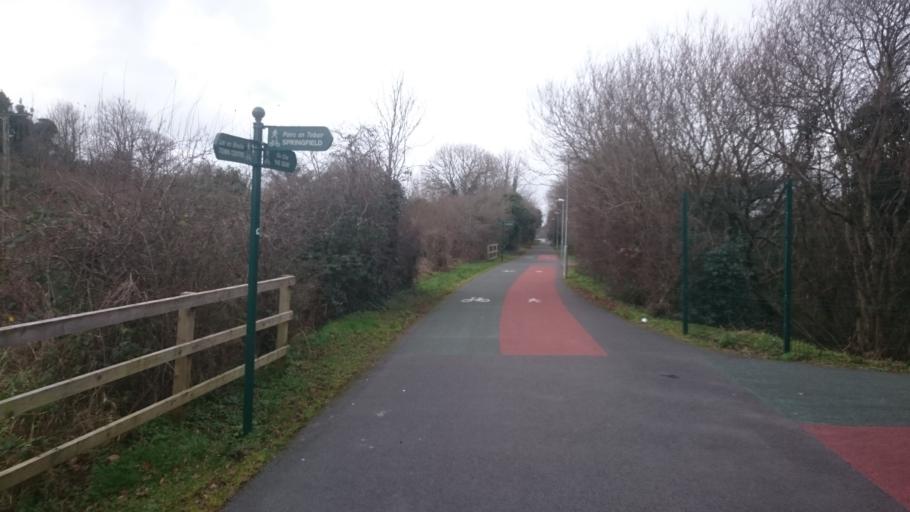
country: IE
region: Connaught
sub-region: Maigh Eo
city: Westport
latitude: 53.7953
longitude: -9.5448
